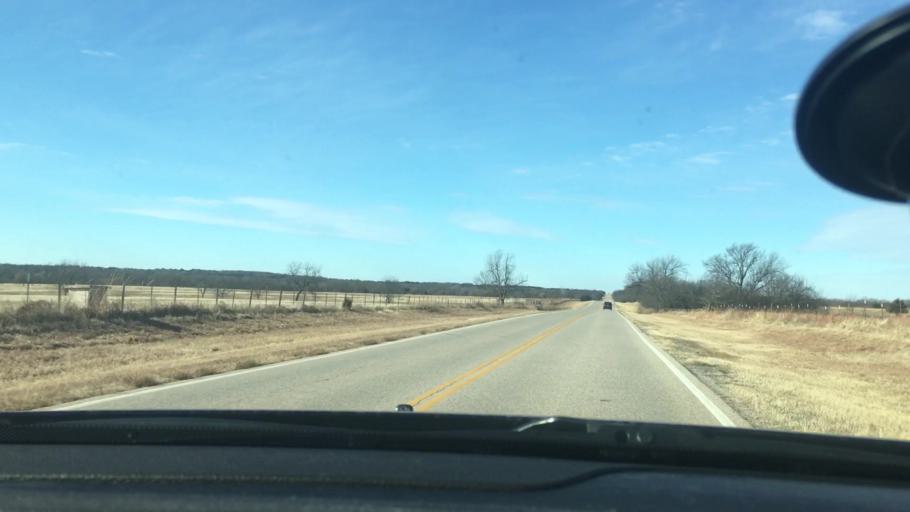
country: US
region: Oklahoma
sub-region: Garvin County
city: Stratford
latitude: 34.9860
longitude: -96.9939
